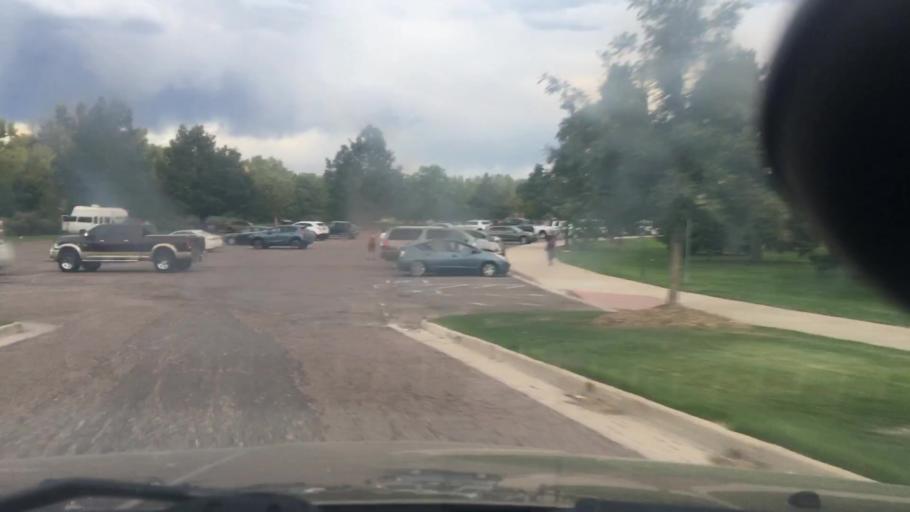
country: US
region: Colorado
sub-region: Arapahoe County
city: Glendale
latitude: 39.6671
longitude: -104.9070
